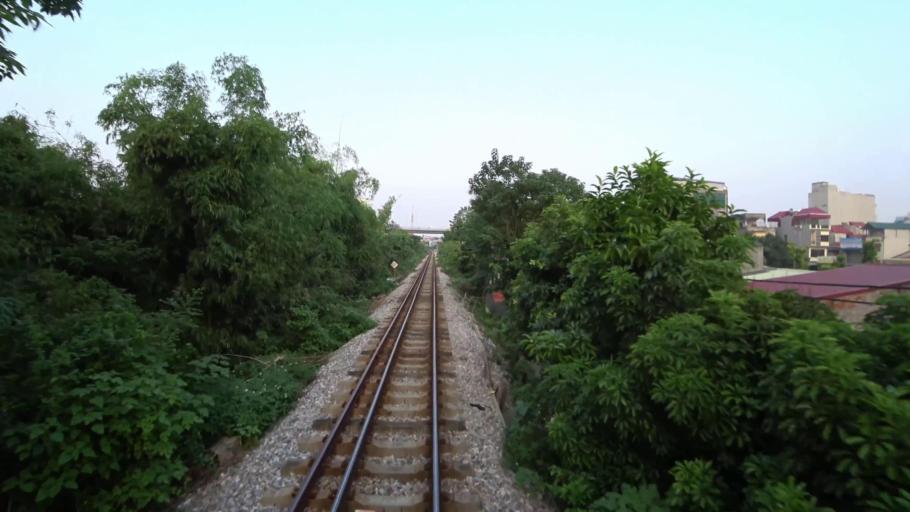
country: VN
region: Ha Noi
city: Trau Quy
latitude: 21.0715
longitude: 105.9027
